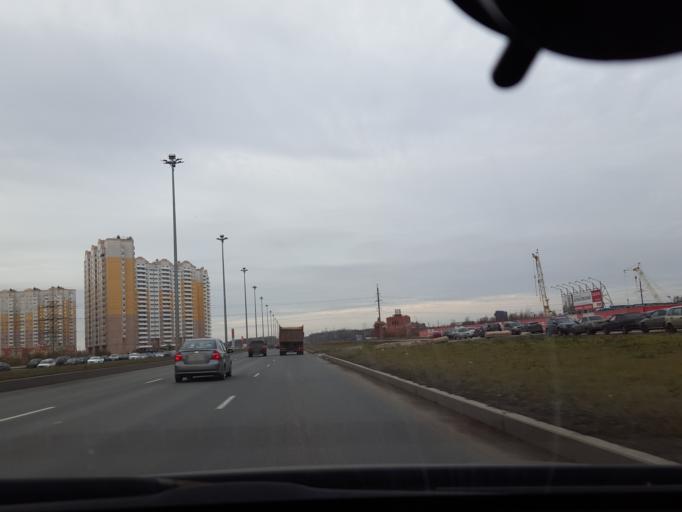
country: RU
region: St.-Petersburg
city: Kolomyagi
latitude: 60.0339
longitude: 30.2492
